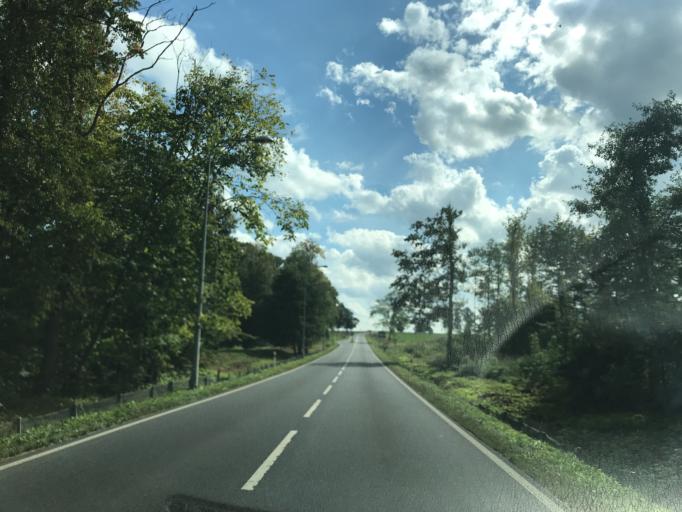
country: PL
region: Warmian-Masurian Voivodeship
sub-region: Powiat ilawski
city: Lubawa
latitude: 53.4233
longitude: 19.7796
